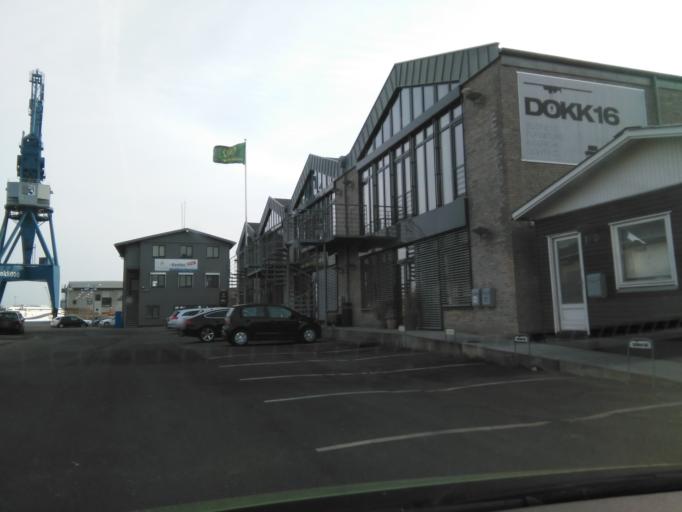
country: DK
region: Central Jutland
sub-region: Arhus Kommune
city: Arhus
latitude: 56.1547
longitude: 10.2198
